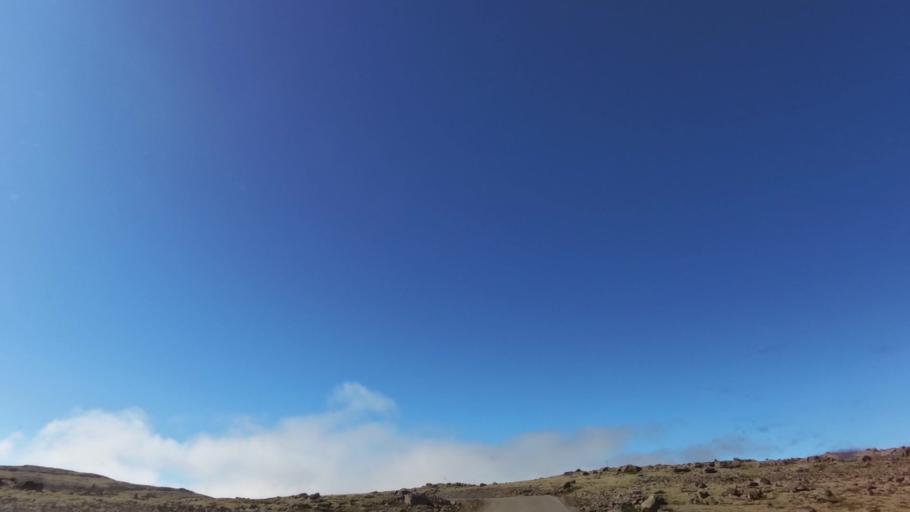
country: IS
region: West
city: Olafsvik
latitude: 65.5505
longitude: -24.2100
